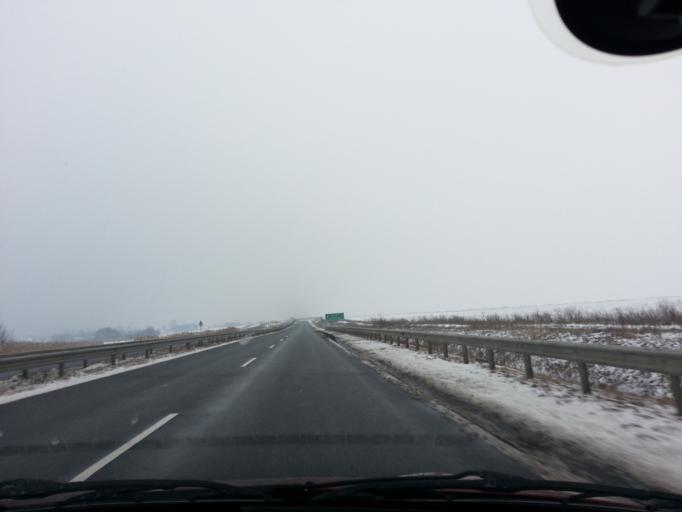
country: HU
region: Nograd
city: Szurdokpuspoki
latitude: 47.8579
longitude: 19.6755
